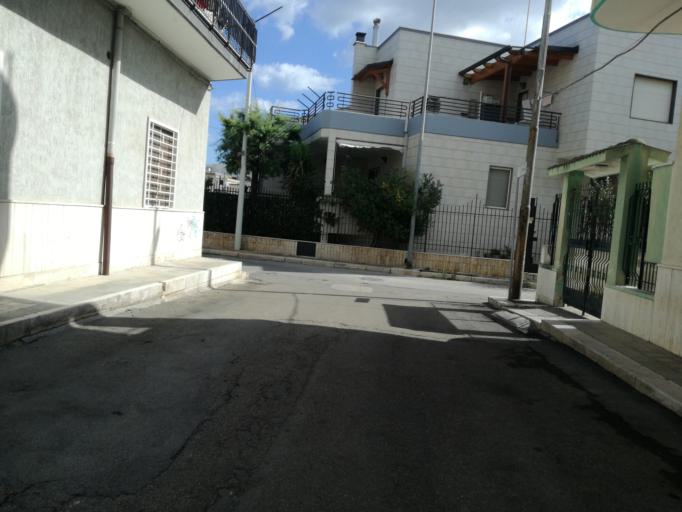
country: IT
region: Apulia
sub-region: Provincia di Bari
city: Triggiano
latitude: 41.0650
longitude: 16.9287
